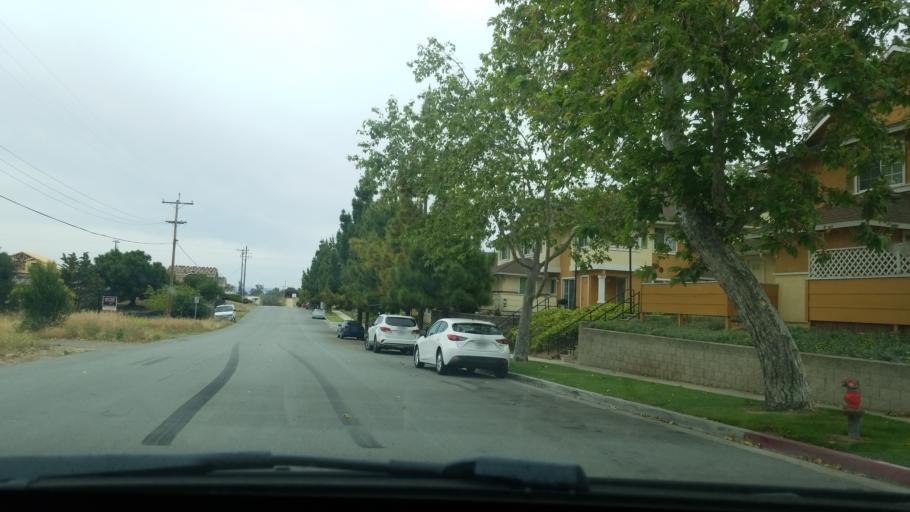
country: US
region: California
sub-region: San Luis Obispo County
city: Nipomo
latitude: 35.0322
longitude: -120.4875
